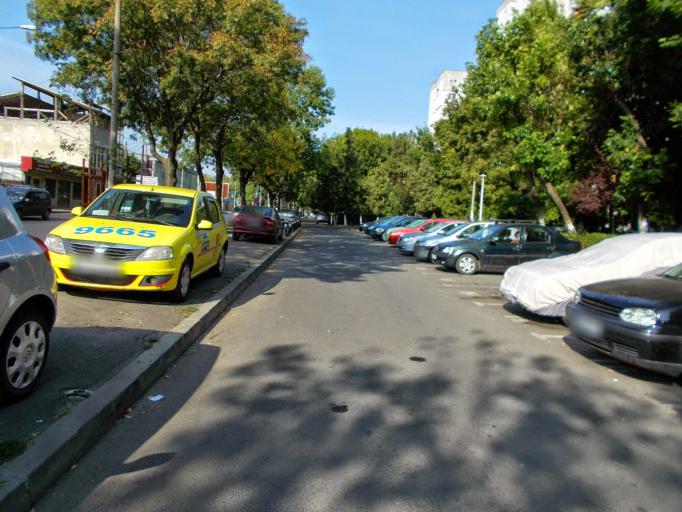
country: RO
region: Ilfov
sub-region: Comuna Jilava
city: Jilava
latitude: 44.3772
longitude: 26.1048
